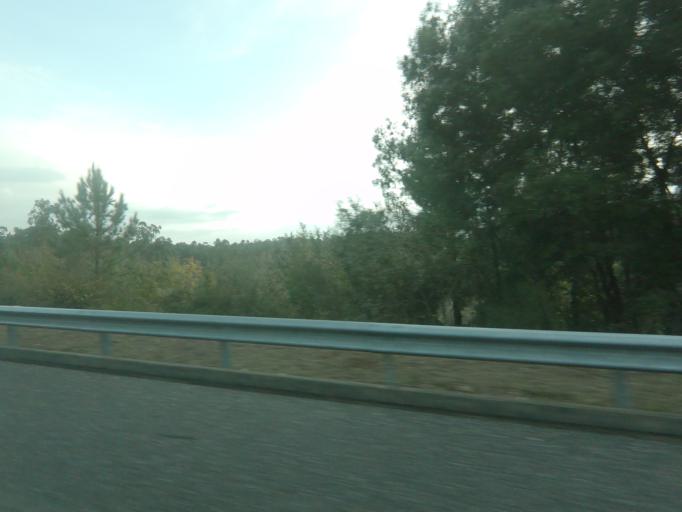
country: ES
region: Galicia
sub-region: Provincia de Pontevedra
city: Tui
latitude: 42.0747
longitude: -8.6397
